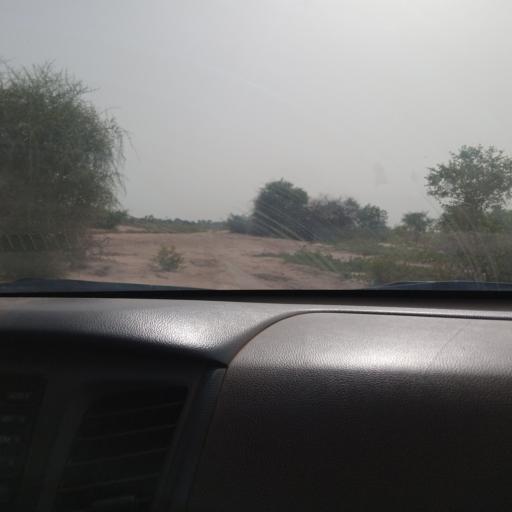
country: ML
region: Mopti
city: Tenenkou
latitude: 14.2099
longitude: -5.0111
